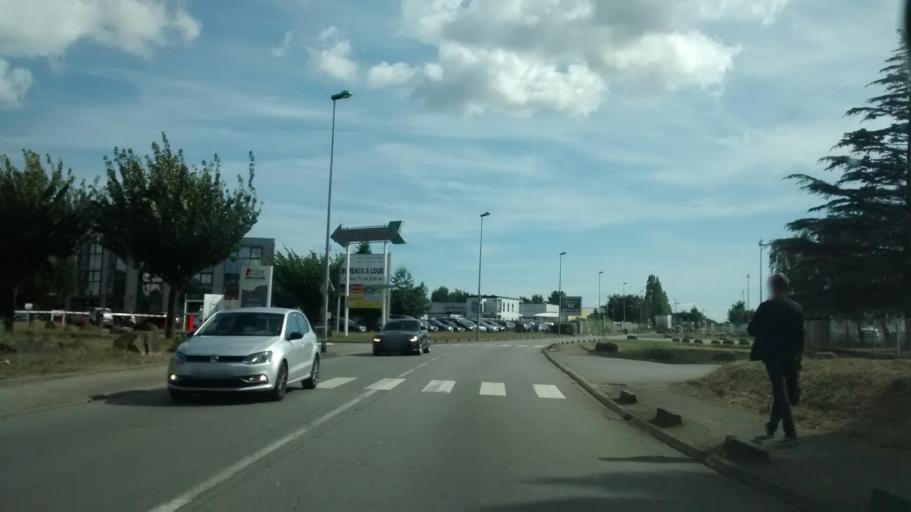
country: FR
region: Pays de la Loire
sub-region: Departement de la Loire-Atlantique
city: Bouguenais
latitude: 47.1575
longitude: -1.5972
